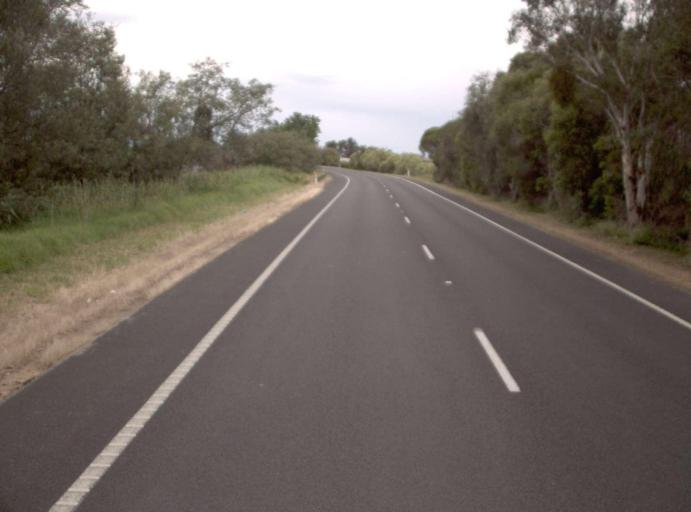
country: AU
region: Victoria
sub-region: East Gippsland
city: Bairnsdale
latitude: -37.8547
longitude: 147.6461
